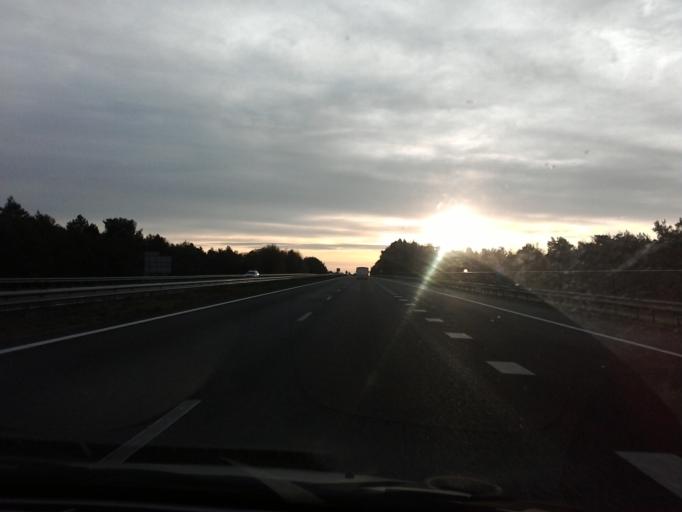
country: NL
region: North Brabant
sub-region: Gemeente Cranendonck
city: Cranendonck
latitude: 51.2936
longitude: 5.6357
